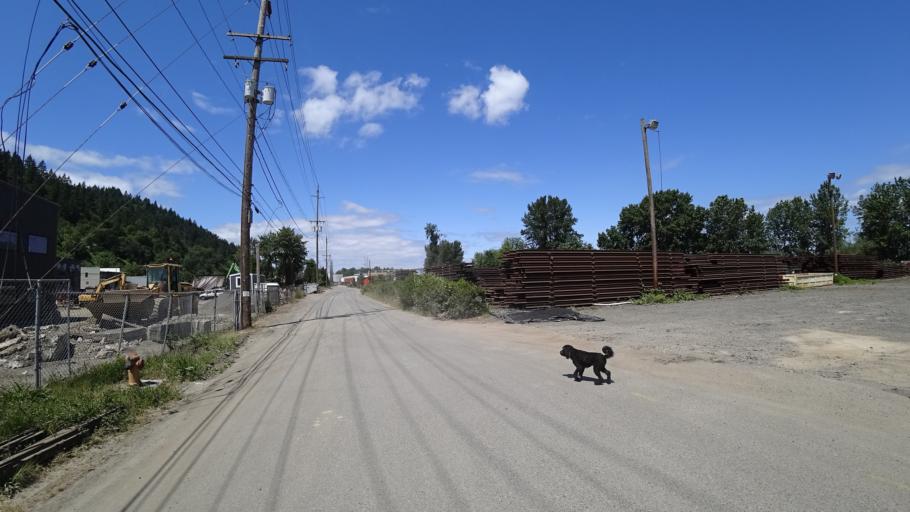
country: US
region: Oregon
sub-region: Washington County
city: Cedar Mill
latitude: 45.5995
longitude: -122.7844
